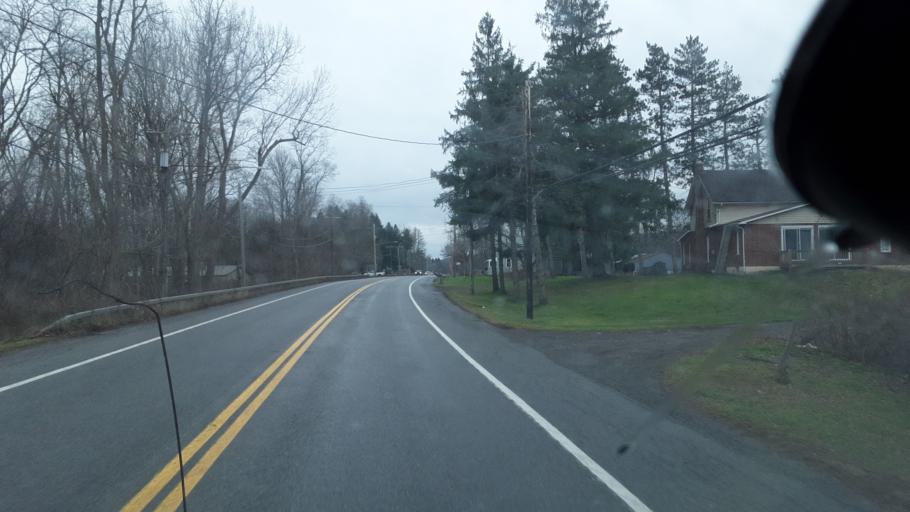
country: US
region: New York
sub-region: Erie County
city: Holland
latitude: 42.7001
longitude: -78.5732
